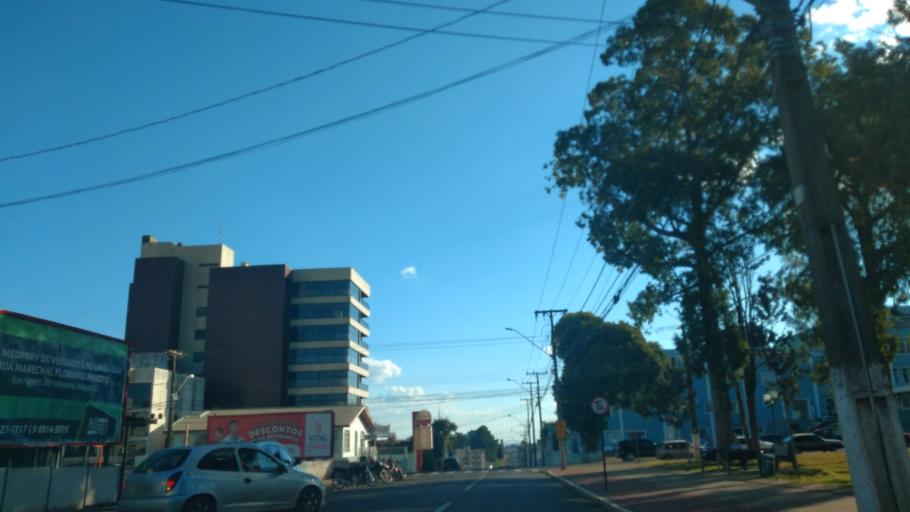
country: BR
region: Parana
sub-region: Guarapuava
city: Guarapuava
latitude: -25.3963
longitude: -51.4621
